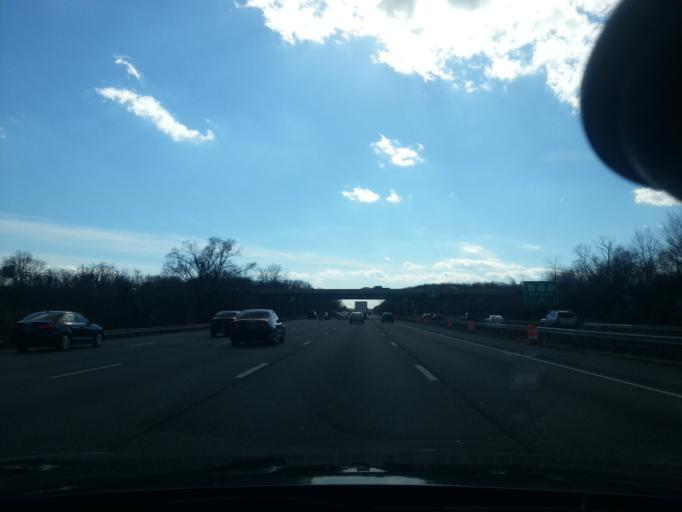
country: US
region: Delaware
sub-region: New Castle County
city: Newport
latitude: 39.7039
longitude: -75.6040
